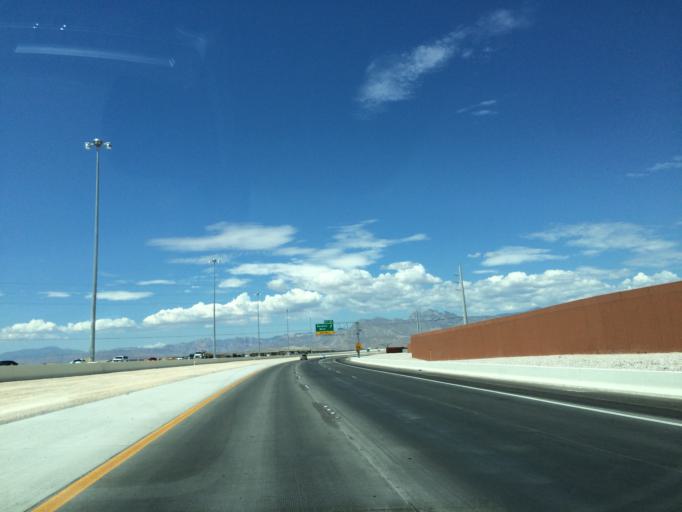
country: US
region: Nevada
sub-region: Clark County
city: North Las Vegas
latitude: 36.2775
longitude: -115.1964
